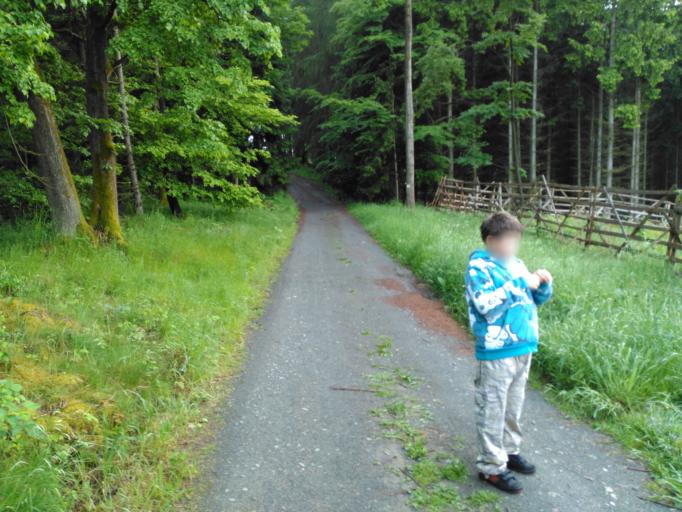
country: CZ
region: Central Bohemia
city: Hudlice
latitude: 49.9643
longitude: 13.9319
